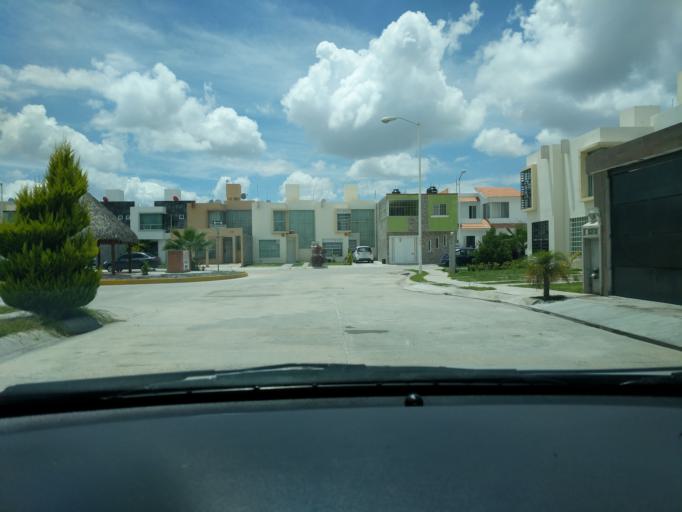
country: MX
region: San Luis Potosi
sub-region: San Luis Potosi
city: Fraccion Milpillas
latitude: 22.2161
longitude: -100.9383
